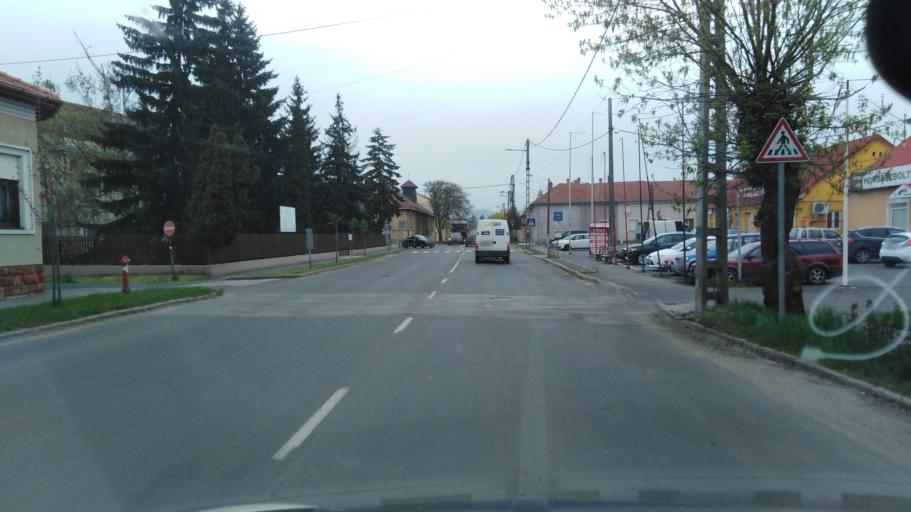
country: HU
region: Nograd
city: Balassagyarmat
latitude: 48.0728
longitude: 19.2964
